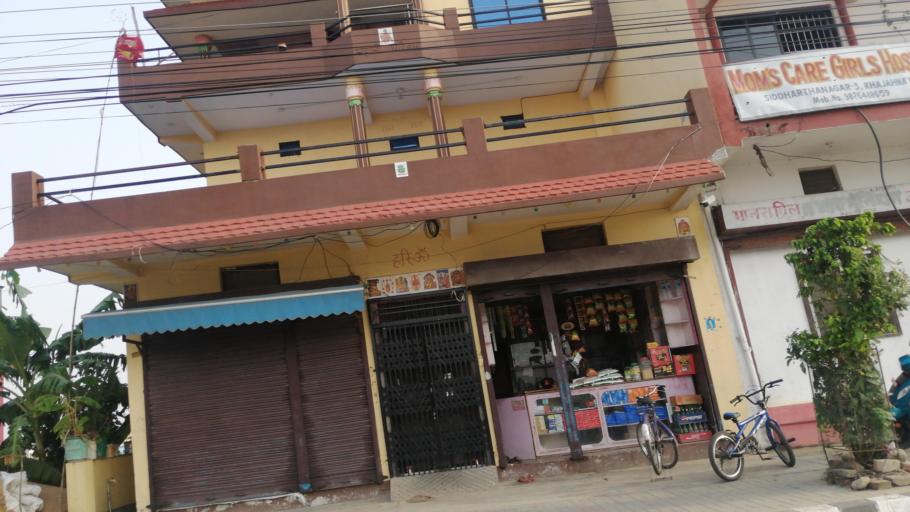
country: NP
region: Western Region
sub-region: Lumbini Zone
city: Bhairahawa
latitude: 27.4977
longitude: 83.4550
